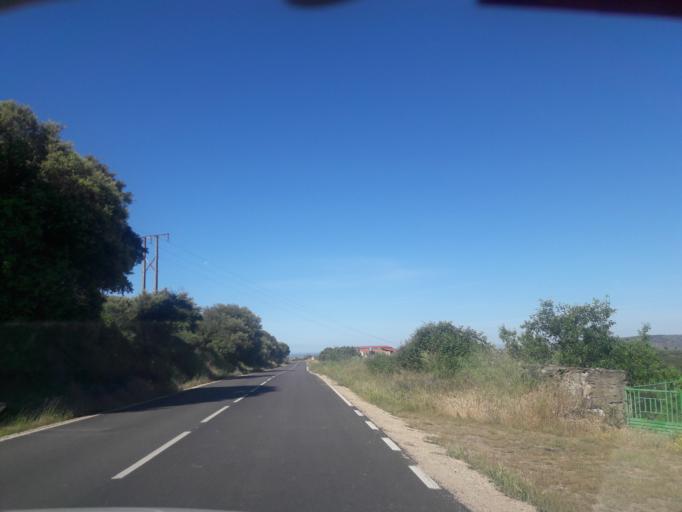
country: ES
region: Castille and Leon
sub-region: Provincia de Salamanca
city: Saucelle
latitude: 41.0436
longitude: -6.7554
